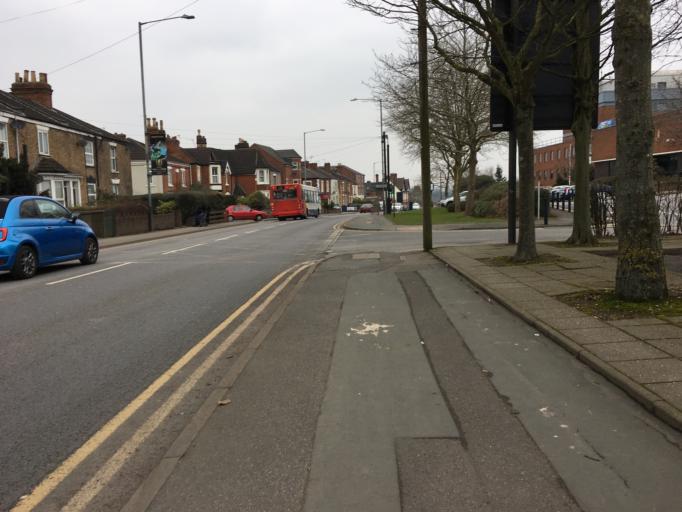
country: GB
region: England
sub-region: Warwickshire
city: Rugby
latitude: 52.3764
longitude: -1.2649
